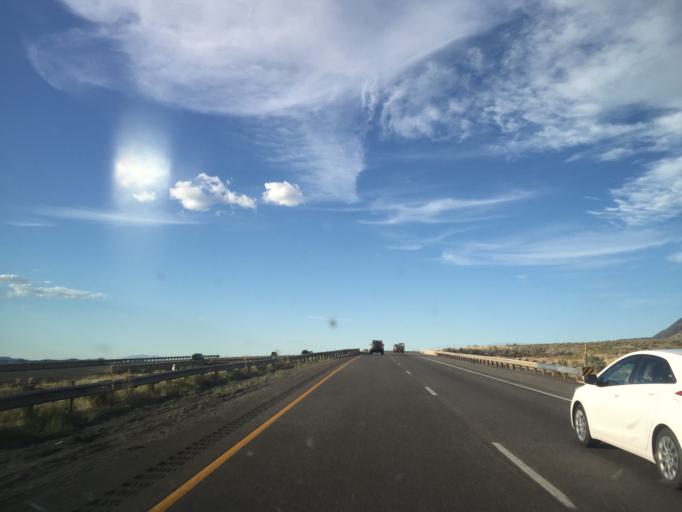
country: US
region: Utah
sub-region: Juab County
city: Mona
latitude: 39.7919
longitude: -111.8383
